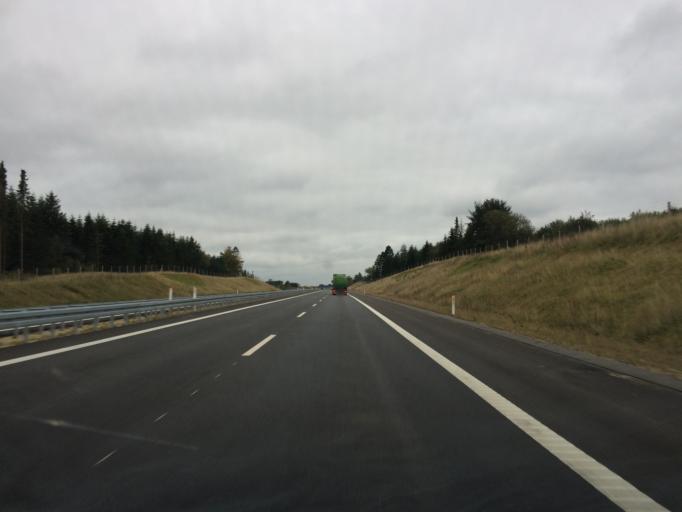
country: DK
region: Central Jutland
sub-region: Silkeborg Kommune
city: Silkeborg
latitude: 56.1751
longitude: 9.4778
